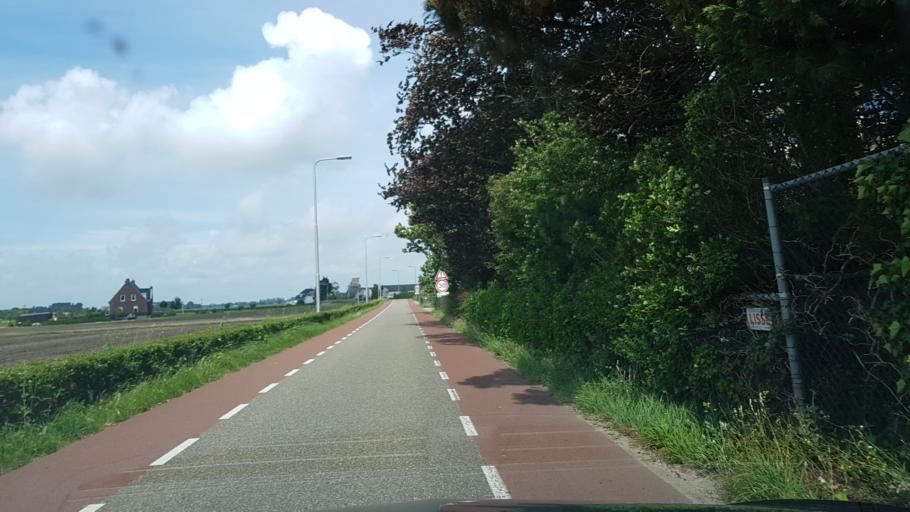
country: NL
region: South Holland
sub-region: Gemeente Lisse
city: Lisse
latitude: 52.2722
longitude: 4.5631
